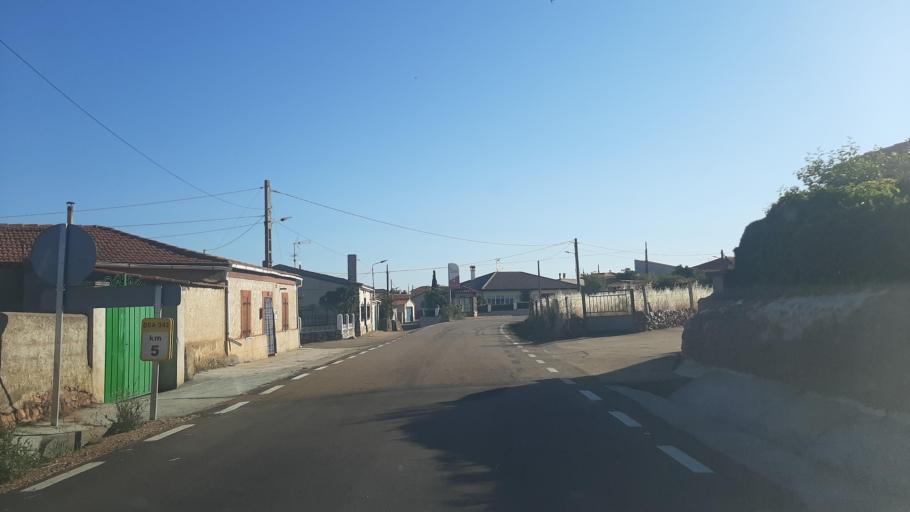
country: ES
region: Castille and Leon
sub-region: Provincia de Salamanca
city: Cabrillas
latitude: 40.6966
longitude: -6.1882
